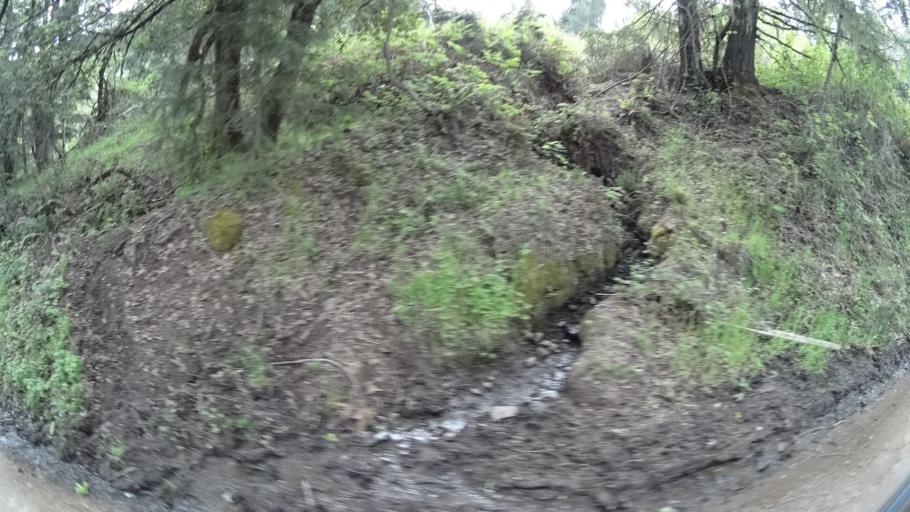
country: US
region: California
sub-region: Humboldt County
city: Redway
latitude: 40.1748
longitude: -123.5702
